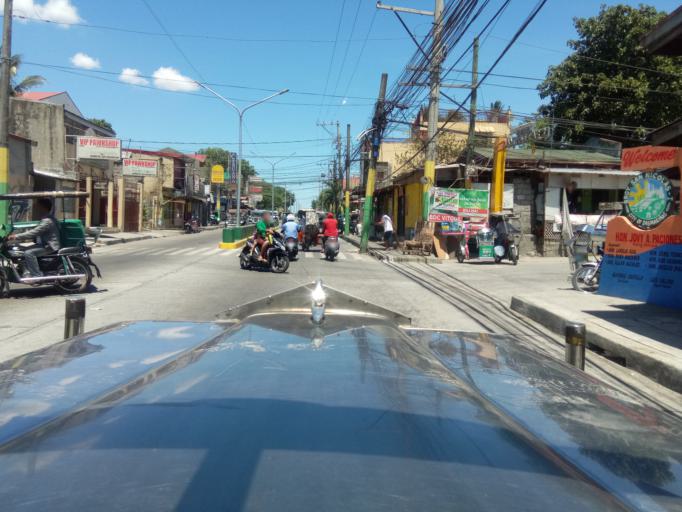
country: PH
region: Calabarzon
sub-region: Province of Cavite
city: Dasmarinas
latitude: 14.3181
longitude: 120.9704
